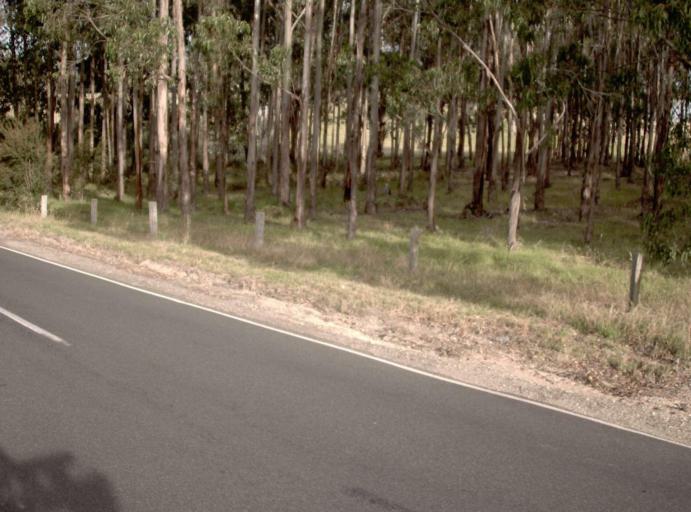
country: AU
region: Victoria
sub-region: Wellington
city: Sale
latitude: -37.9260
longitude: 146.9943
